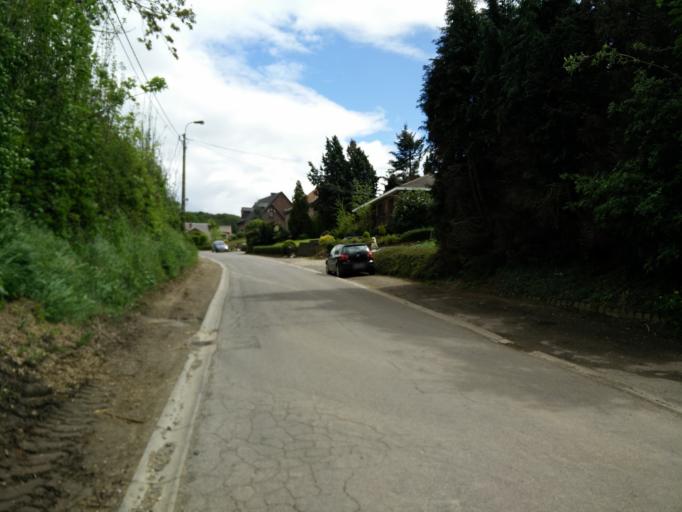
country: BE
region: Flanders
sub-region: Provincie Limburg
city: Sint-Pieters-Voeren
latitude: 50.7340
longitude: 5.7736
